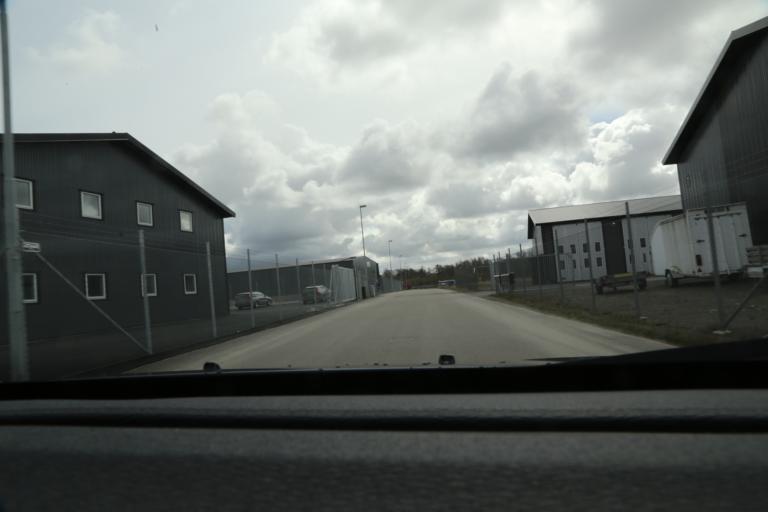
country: SE
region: Halland
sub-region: Varbergs Kommun
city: Varberg
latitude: 57.1220
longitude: 12.3025
